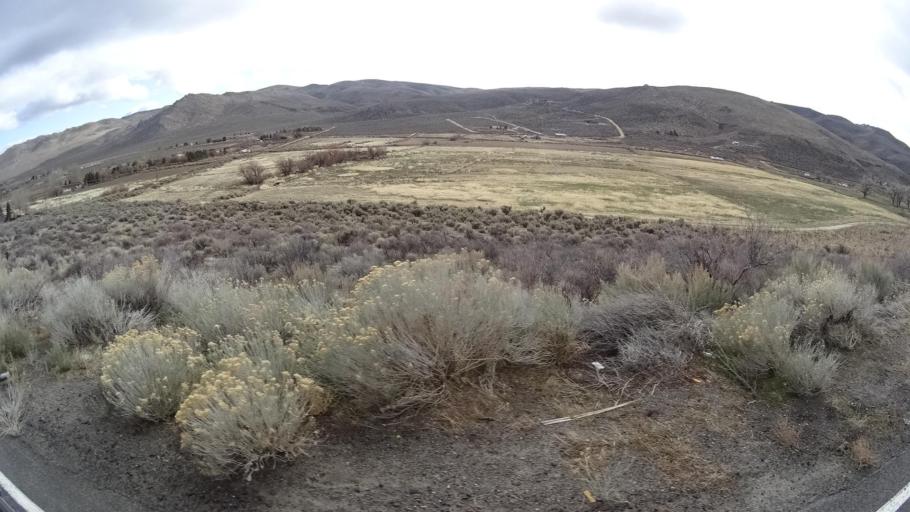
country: US
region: Nevada
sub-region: Washoe County
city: Cold Springs
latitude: 39.8430
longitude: -119.9355
